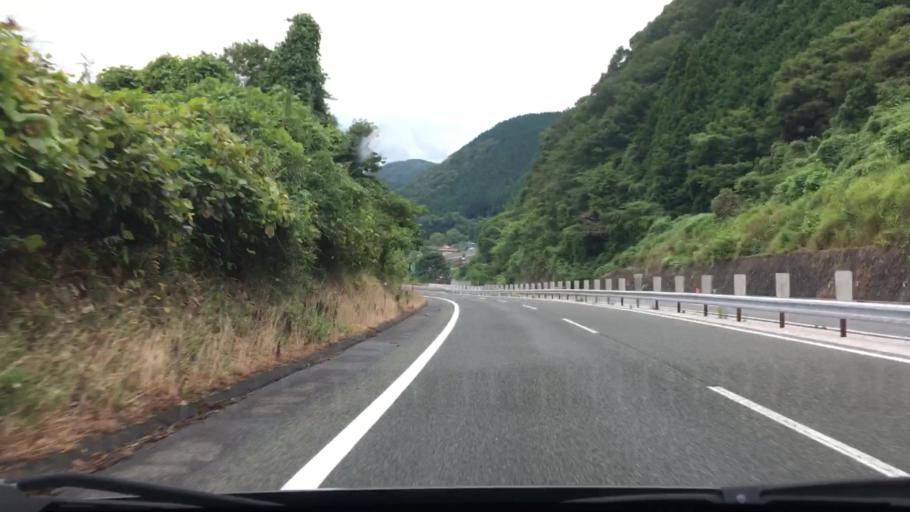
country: JP
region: Okayama
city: Niimi
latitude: 34.9802
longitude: 133.3748
